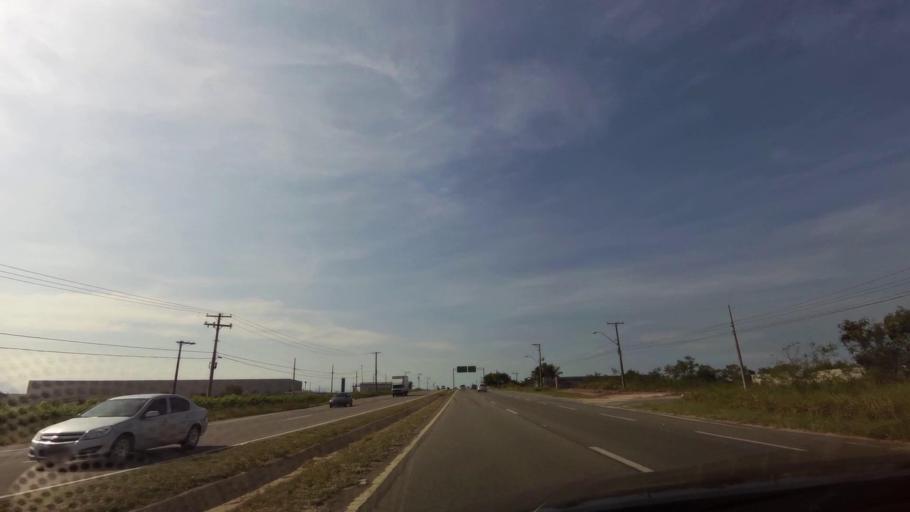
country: BR
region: Espirito Santo
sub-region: Vitoria
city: Vitoria
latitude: -20.4911
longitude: -40.3549
